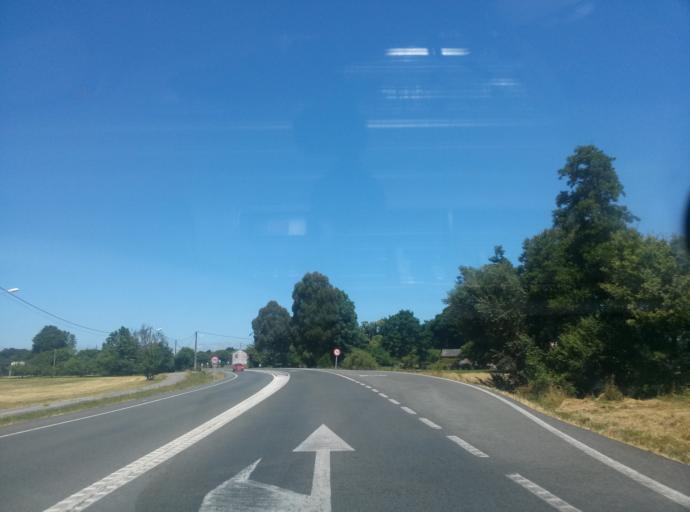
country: ES
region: Galicia
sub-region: Provincia de Lugo
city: Mos
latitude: 43.1728
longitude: -7.4789
